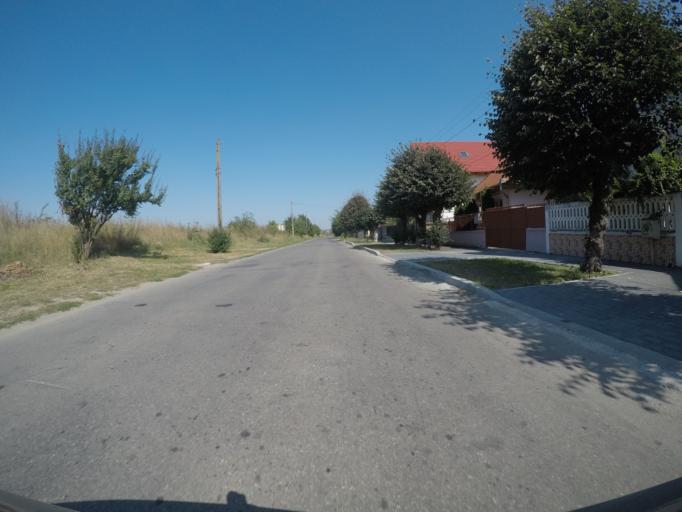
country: RO
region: Brasov
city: Fogarasch
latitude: 45.8246
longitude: 24.9794
